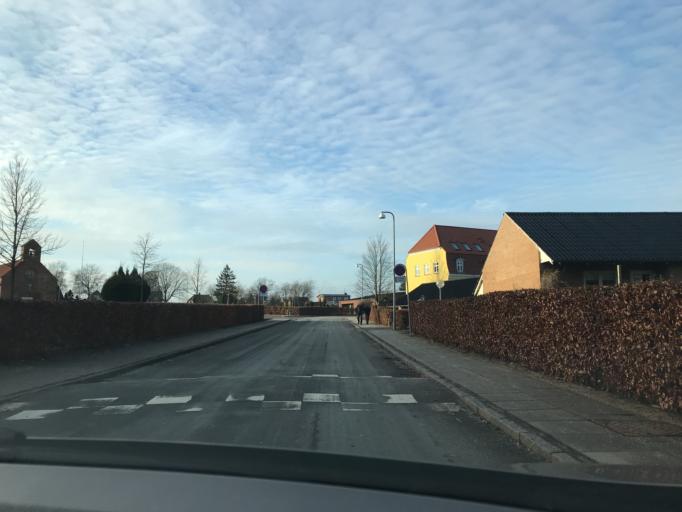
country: DK
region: South Denmark
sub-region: Vejle Kommune
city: Vejle
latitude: 55.6928
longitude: 9.5281
